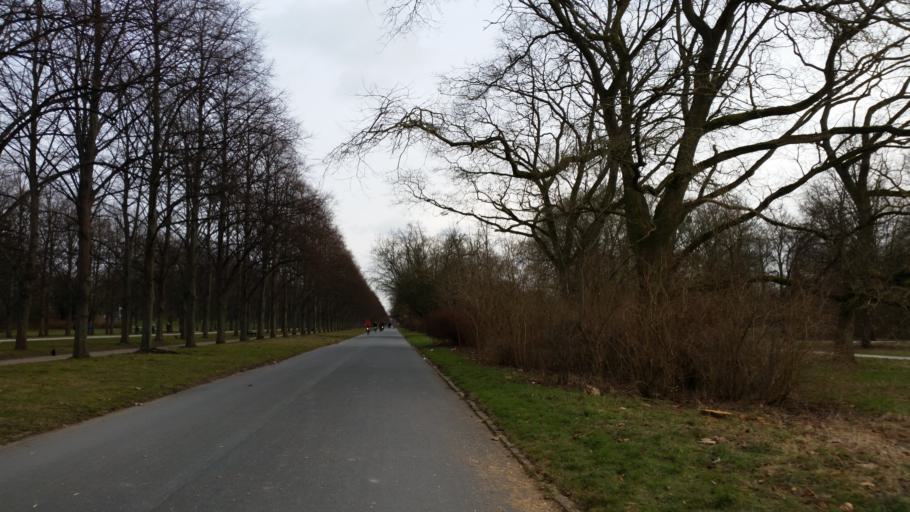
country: DE
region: Lower Saxony
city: Hannover
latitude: 52.3855
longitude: 9.7099
